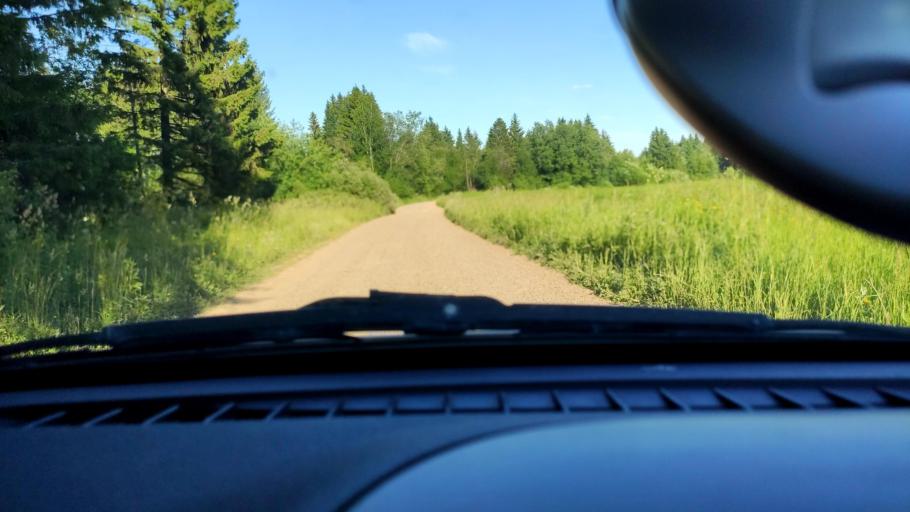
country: RU
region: Perm
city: Bershet'
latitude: 57.6979
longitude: 56.4083
